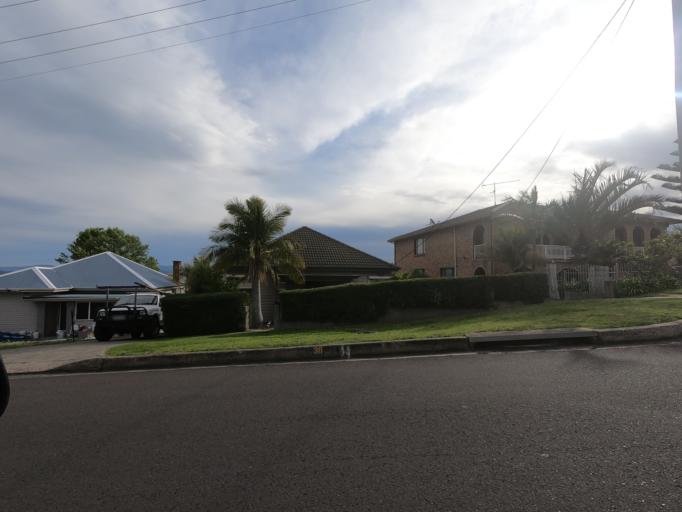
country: AU
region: New South Wales
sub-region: Wollongong
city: Lake Heights
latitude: -34.4869
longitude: 150.8686
